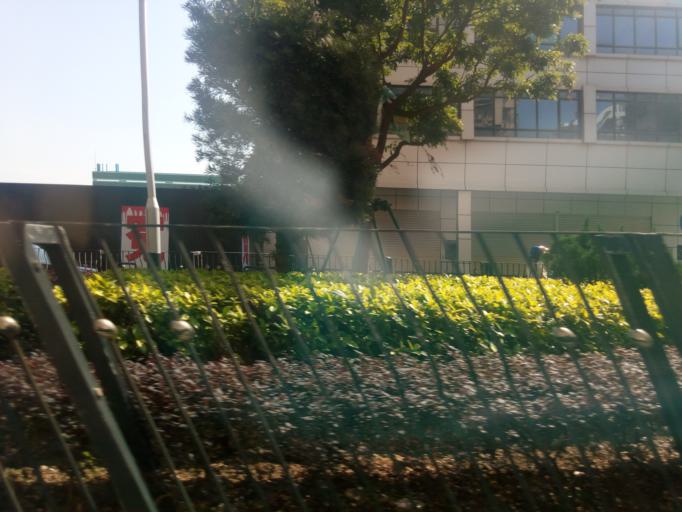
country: MO
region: Macau
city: Macau
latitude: 22.2087
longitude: 113.5571
